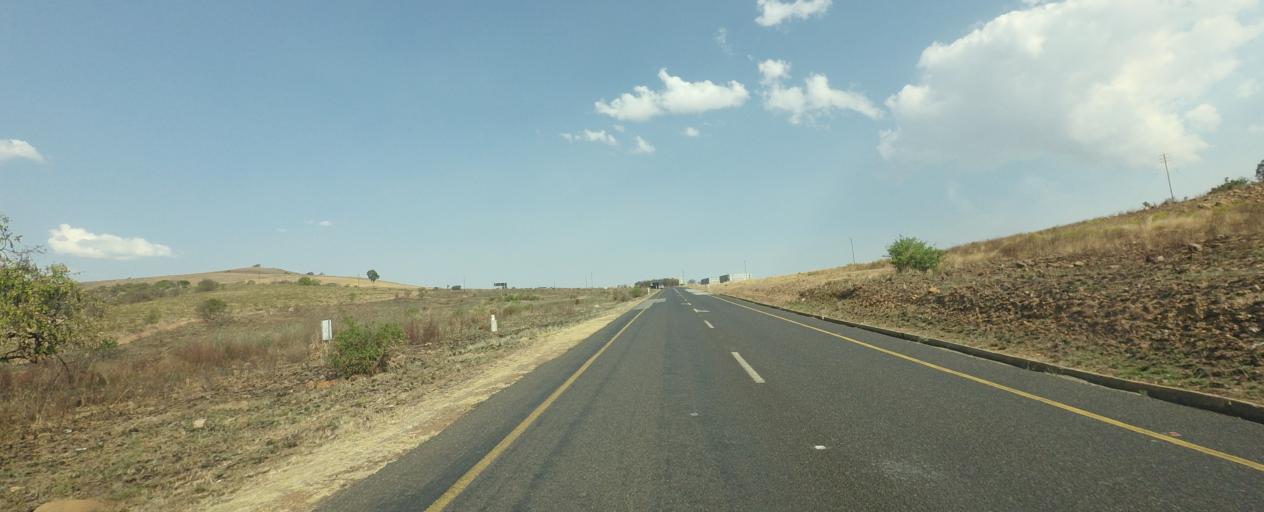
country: ZA
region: Mpumalanga
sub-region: Ehlanzeni District
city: Lydenburg
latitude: -25.1081
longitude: 30.4938
